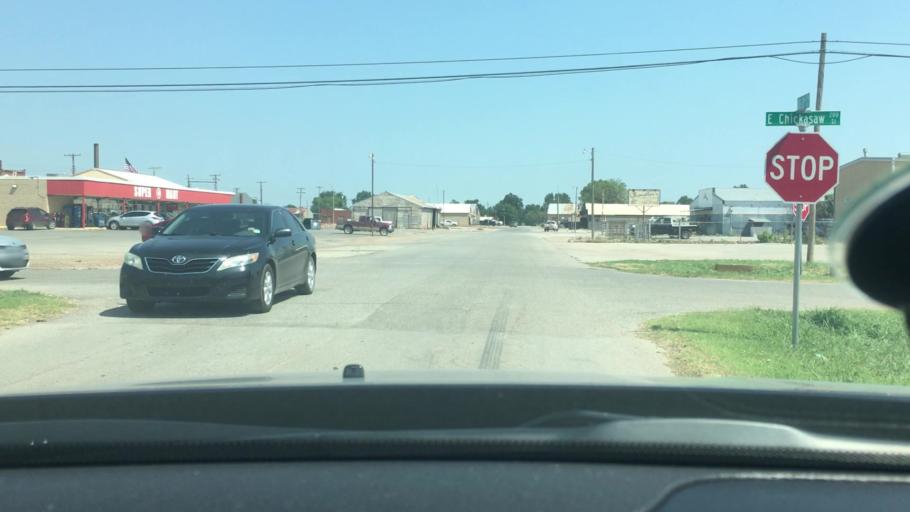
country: US
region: Oklahoma
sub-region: Garvin County
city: Lindsay
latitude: 34.8344
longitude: -97.6013
